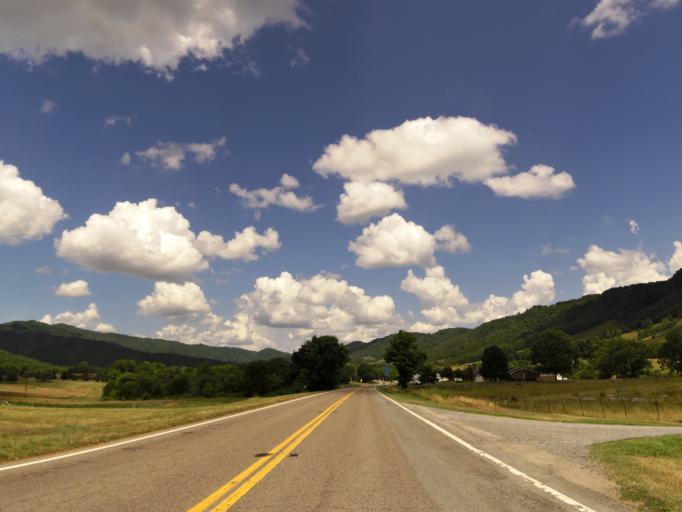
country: US
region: Virginia
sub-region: Lee County
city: Pennington Gap
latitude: 36.7006
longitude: -82.9953
